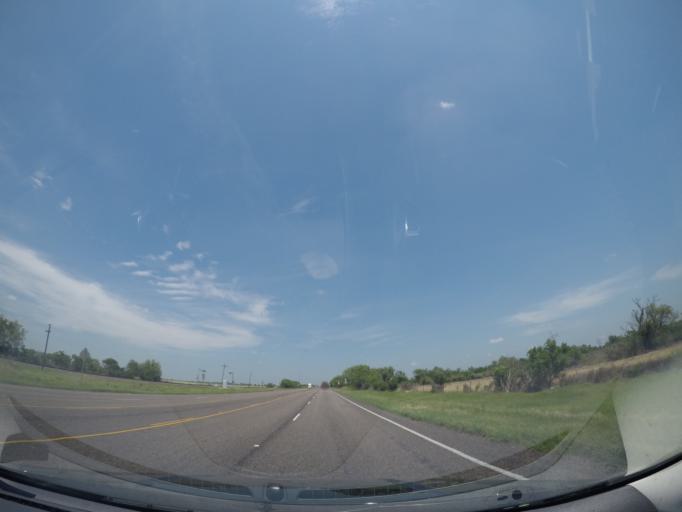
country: US
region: Texas
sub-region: Uvalde County
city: Sabinal
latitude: 29.3118
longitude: -99.5151
